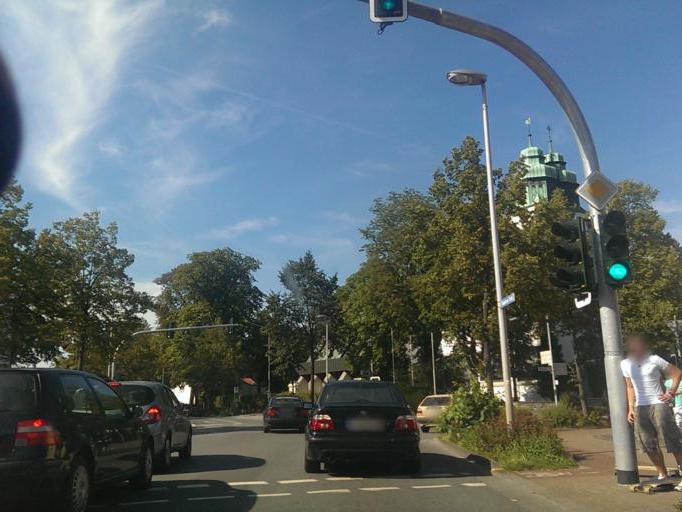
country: DE
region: North Rhine-Westphalia
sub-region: Regierungsbezirk Detmold
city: Hovelhof
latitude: 51.8202
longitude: 8.6587
